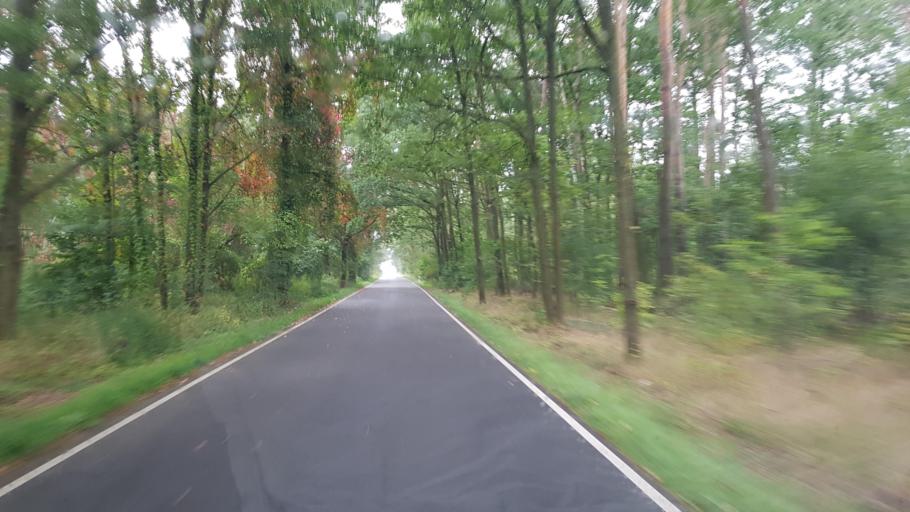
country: DE
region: Brandenburg
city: Lindenau
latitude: 51.4006
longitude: 13.7374
